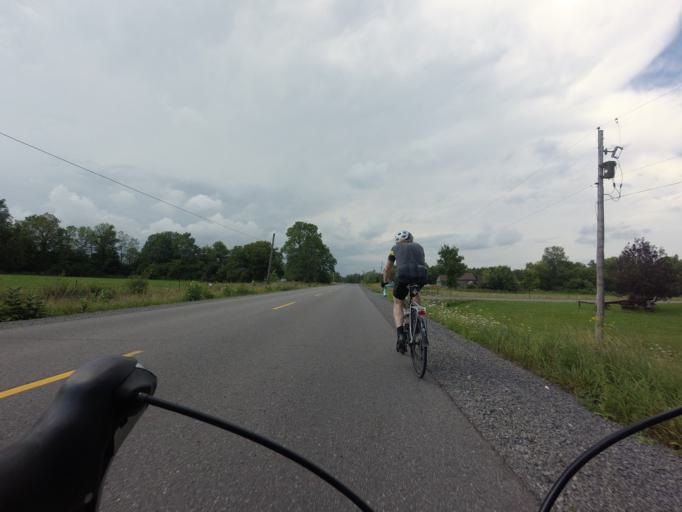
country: CA
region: Ontario
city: Brockville
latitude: 44.8002
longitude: -75.7915
